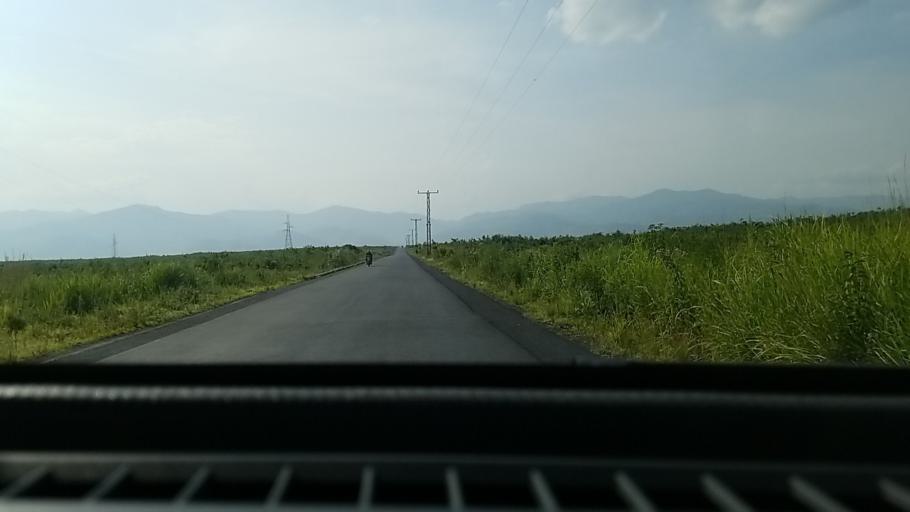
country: CD
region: Nord Kivu
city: Sake
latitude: -1.5971
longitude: 29.1079
